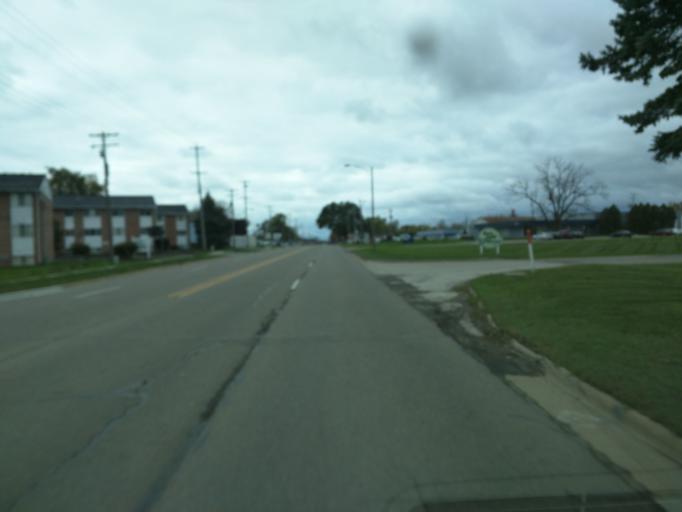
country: US
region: Michigan
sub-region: Ingham County
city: Edgemont Park
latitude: 42.7668
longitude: -84.5908
